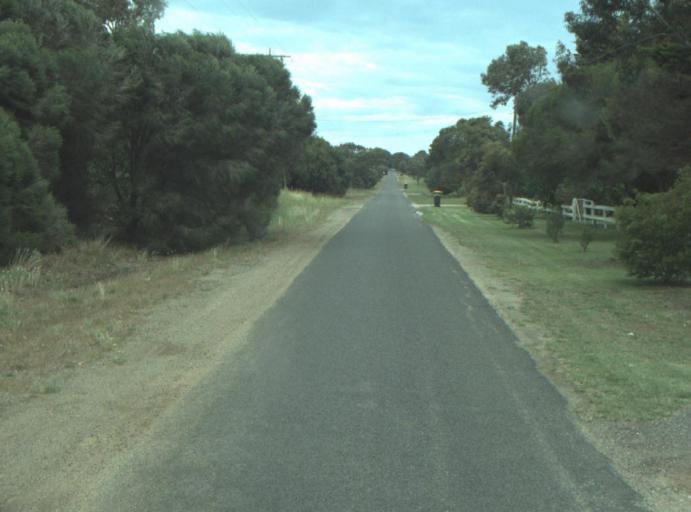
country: AU
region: Victoria
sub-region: Greater Geelong
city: Leopold
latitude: -38.2114
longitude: 144.4505
